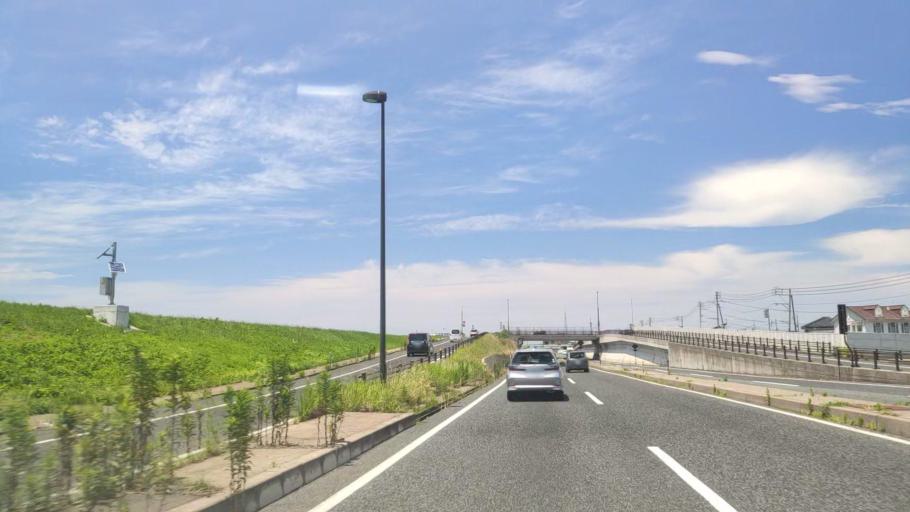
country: JP
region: Tottori
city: Tottori
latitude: 35.5033
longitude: 134.2178
